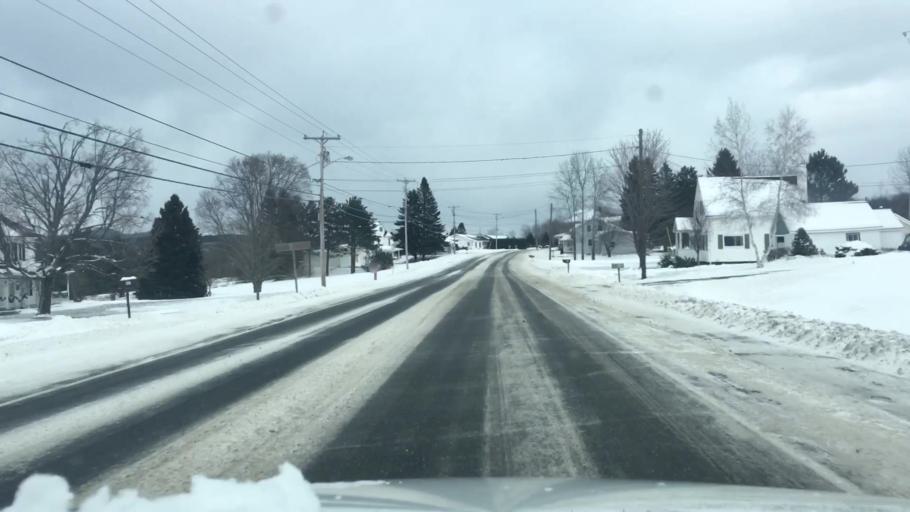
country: US
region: Maine
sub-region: Aroostook County
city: Madawaska
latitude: 47.3464
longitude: -68.2615
